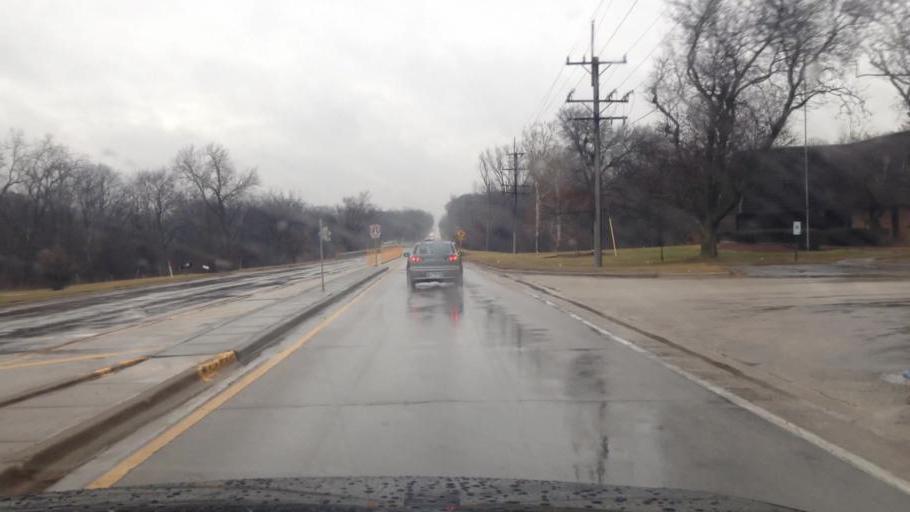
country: US
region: Illinois
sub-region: Will County
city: Ingalls Park
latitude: 41.5245
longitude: -88.0048
